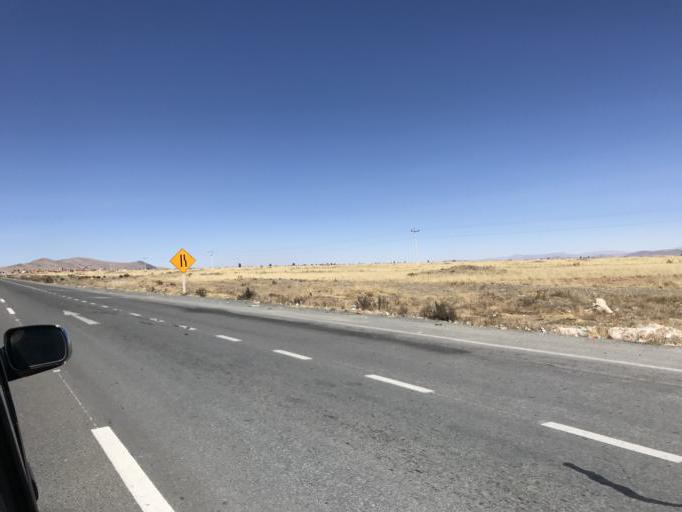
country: BO
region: La Paz
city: Batallas
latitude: -16.3195
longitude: -68.4381
